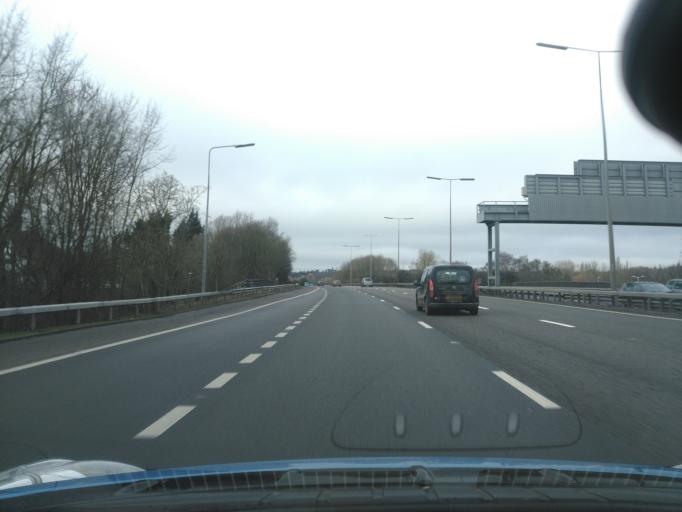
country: GB
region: England
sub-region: Hertfordshire
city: Hatfield
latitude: 51.7840
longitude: -0.2234
